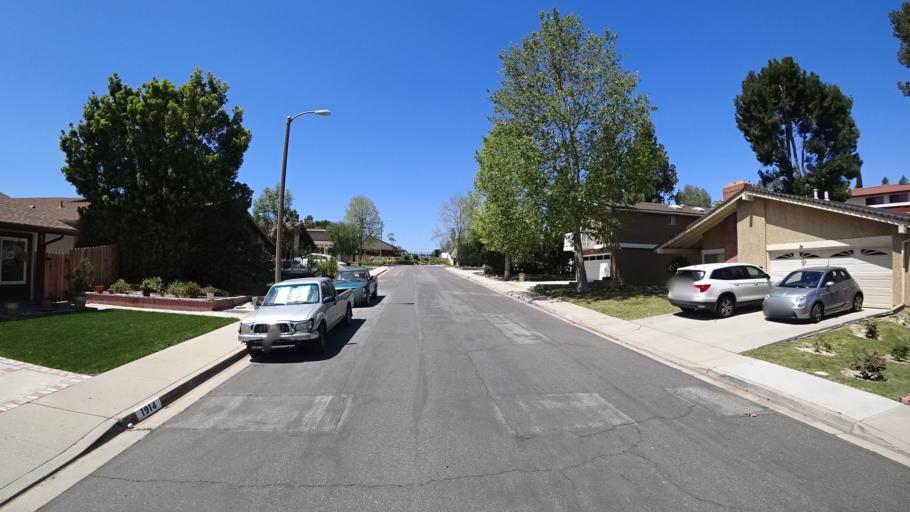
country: US
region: California
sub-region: Ventura County
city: Thousand Oaks
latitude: 34.2182
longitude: -118.8433
